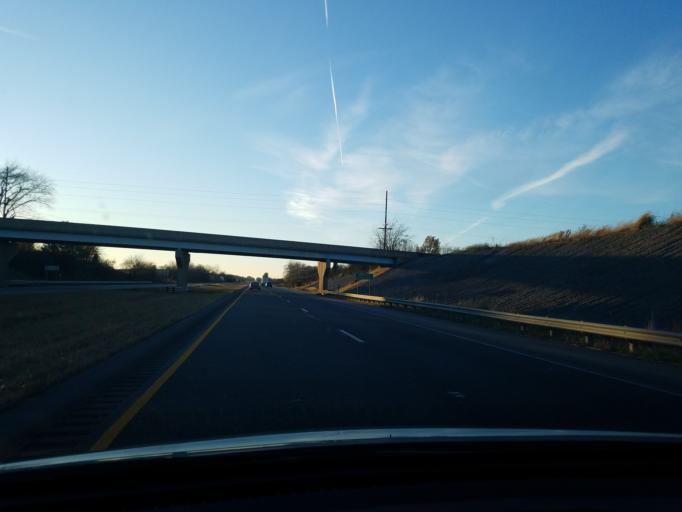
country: US
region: Indiana
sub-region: Gibson County
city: Haubstadt
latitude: 38.1671
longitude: -87.5720
